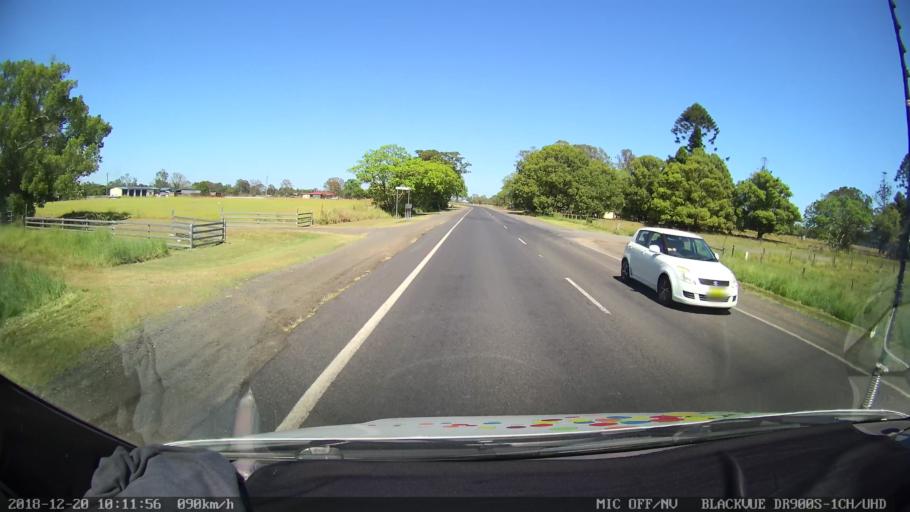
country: AU
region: New South Wales
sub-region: Richmond Valley
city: Casino
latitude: -28.8720
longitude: 153.1510
